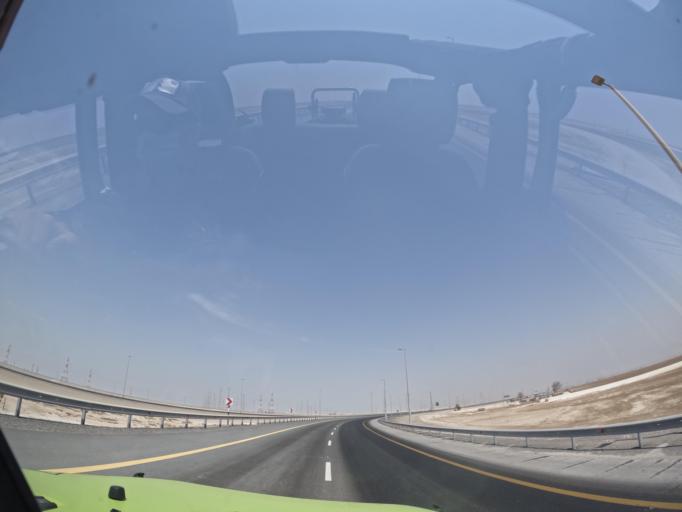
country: AE
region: Abu Dhabi
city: Abu Dhabi
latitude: 24.1485
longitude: 54.2424
